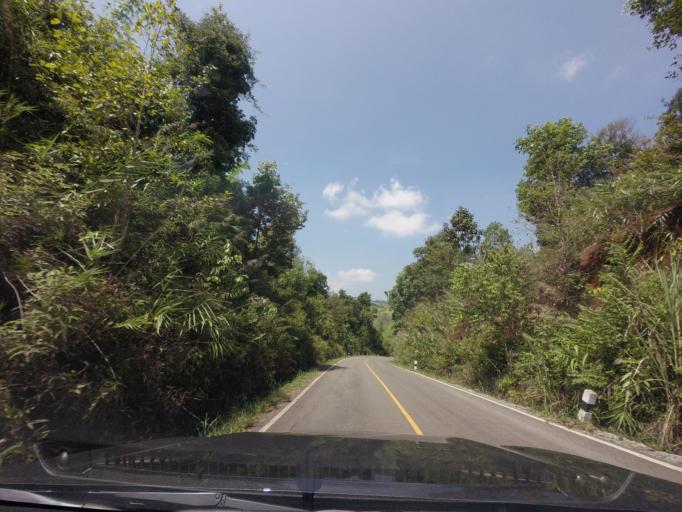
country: TH
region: Loei
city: Na Haeo
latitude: 17.5847
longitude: 100.9067
